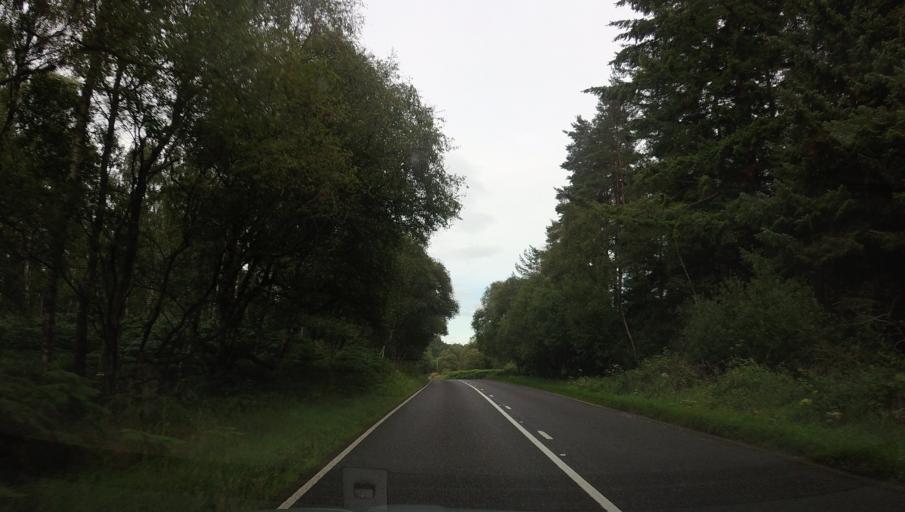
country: GB
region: Scotland
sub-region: Aberdeenshire
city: Torphins
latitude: 57.0642
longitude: -2.5808
